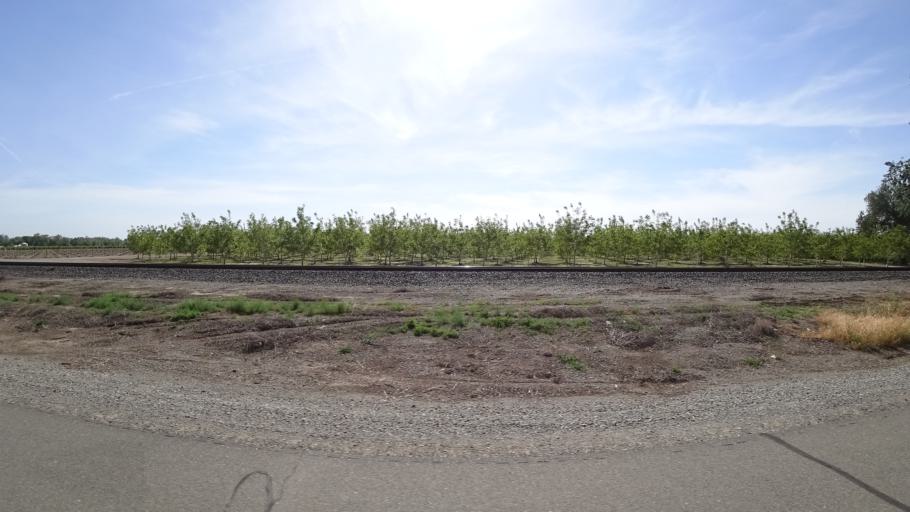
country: US
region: California
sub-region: Tehama County
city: Los Molinos
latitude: 39.9888
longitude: -122.0835
